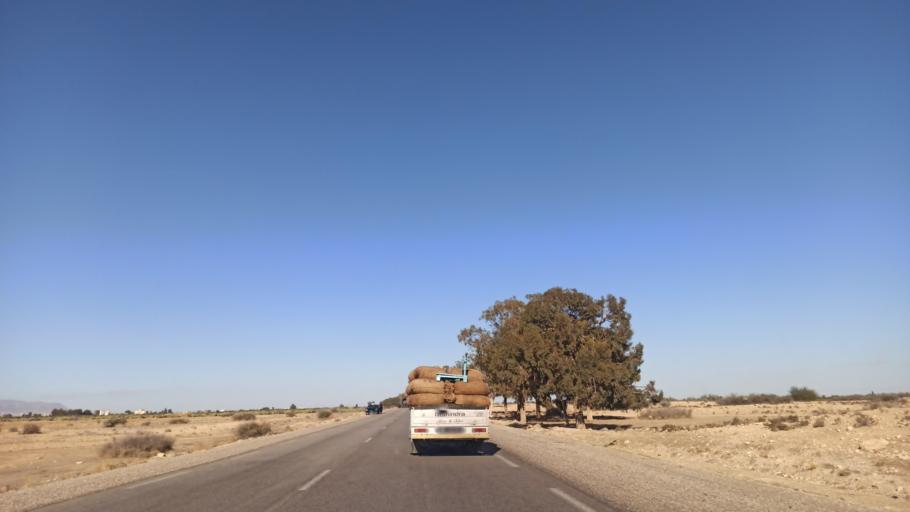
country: TN
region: Sidi Bu Zayd
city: Jilma
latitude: 35.2056
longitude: 9.3787
